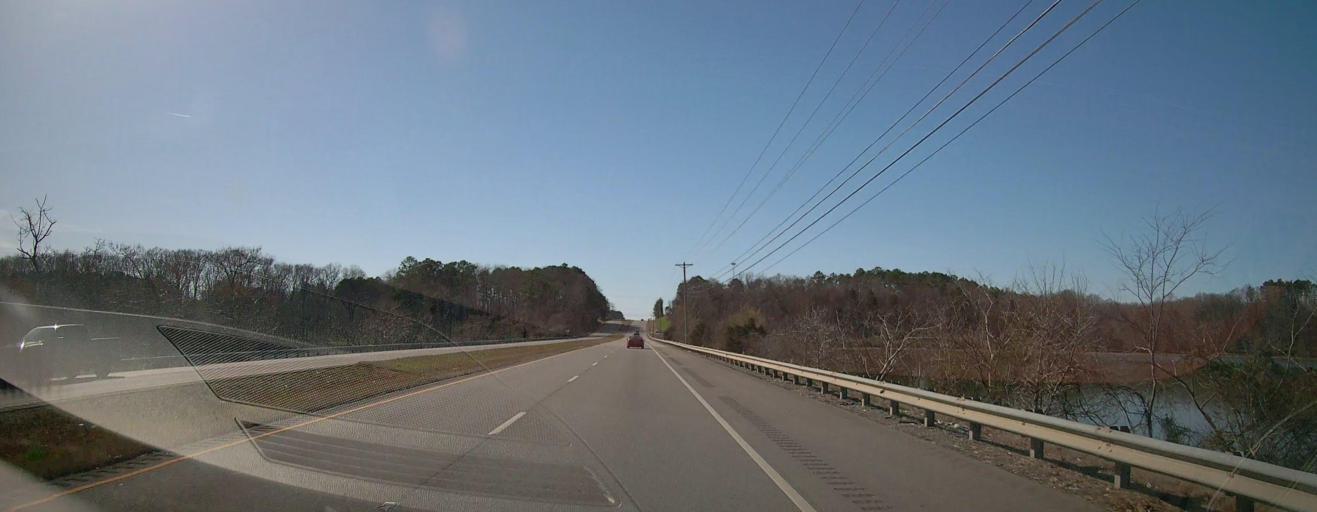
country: US
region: Alabama
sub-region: Lauderdale County
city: Rogersville
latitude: 34.8444
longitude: -87.3741
